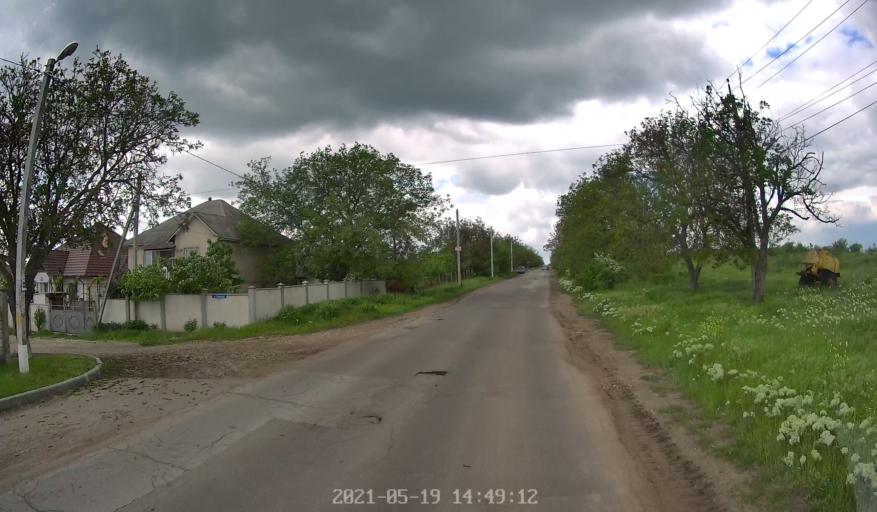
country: MD
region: Chisinau
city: Stauceni
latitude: 47.0481
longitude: 28.9534
